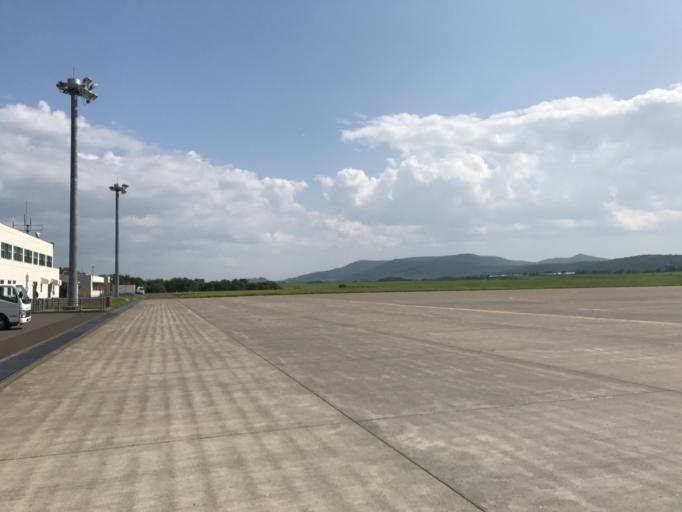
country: JP
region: Hokkaido
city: Mombetsu
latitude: 44.3064
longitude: 143.4066
